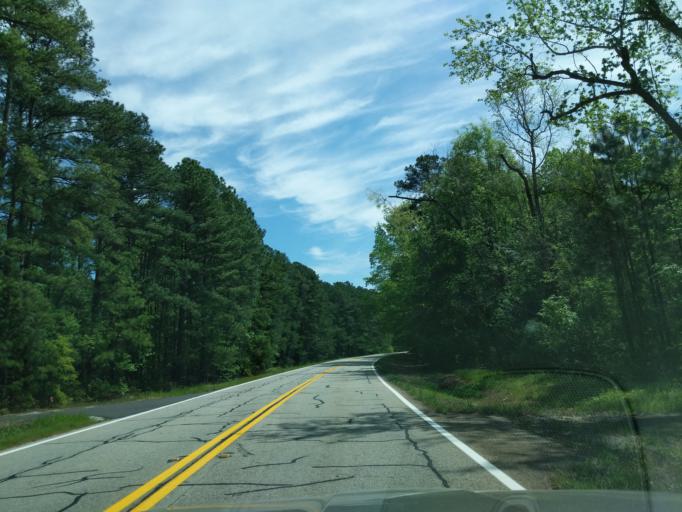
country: US
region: Georgia
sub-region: Columbia County
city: Appling
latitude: 33.6109
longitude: -82.3385
